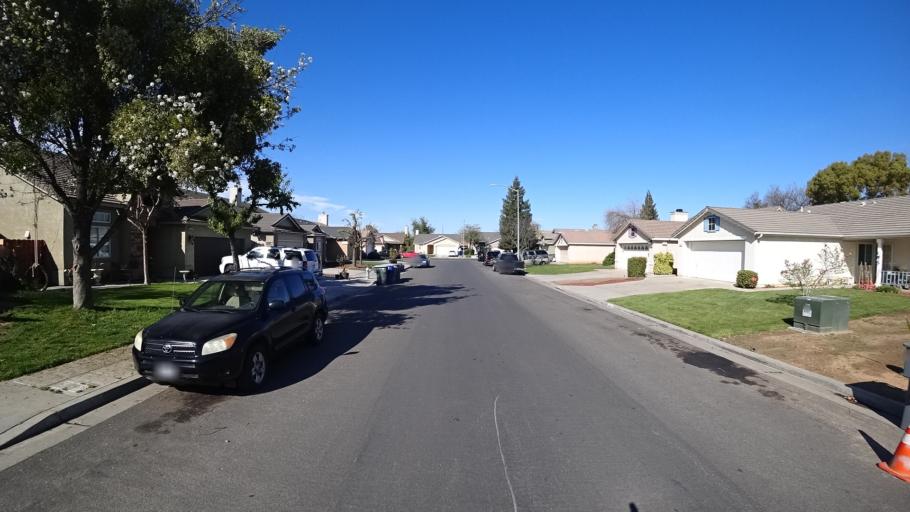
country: US
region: California
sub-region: Fresno County
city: West Park
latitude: 36.7982
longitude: -119.8927
